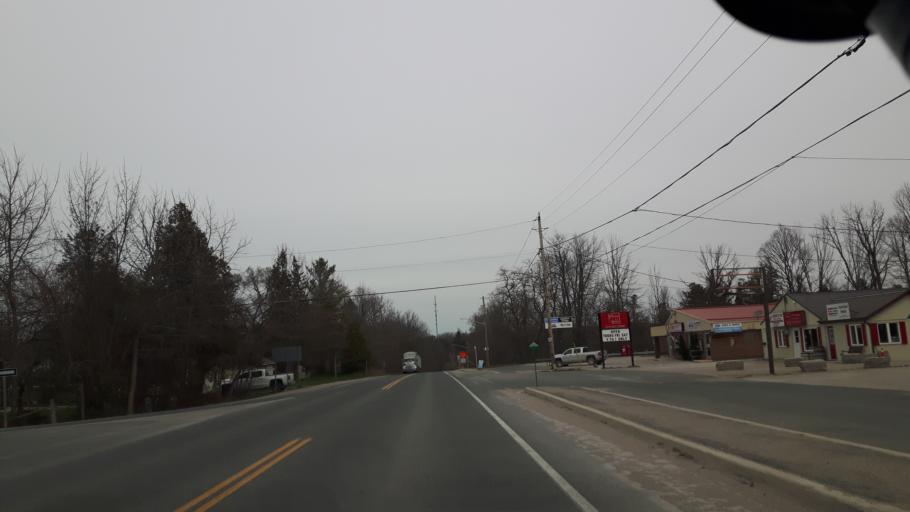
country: CA
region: Ontario
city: Bluewater
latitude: 43.5628
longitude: -81.6968
